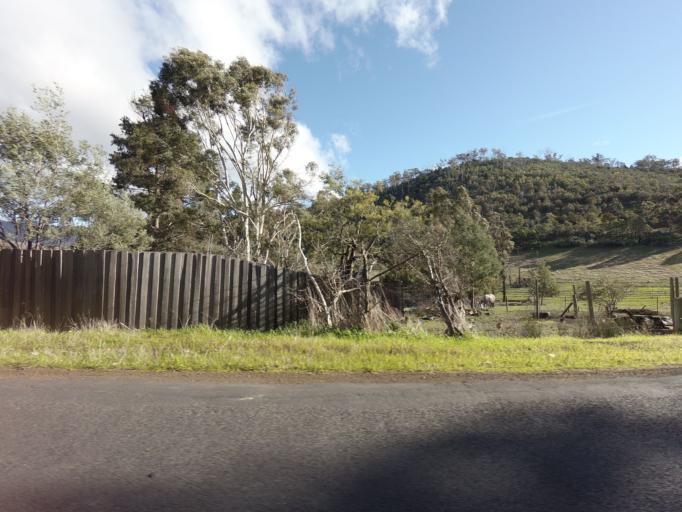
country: AU
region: Tasmania
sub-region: Derwent Valley
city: New Norfolk
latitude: -42.7510
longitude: 147.0461
